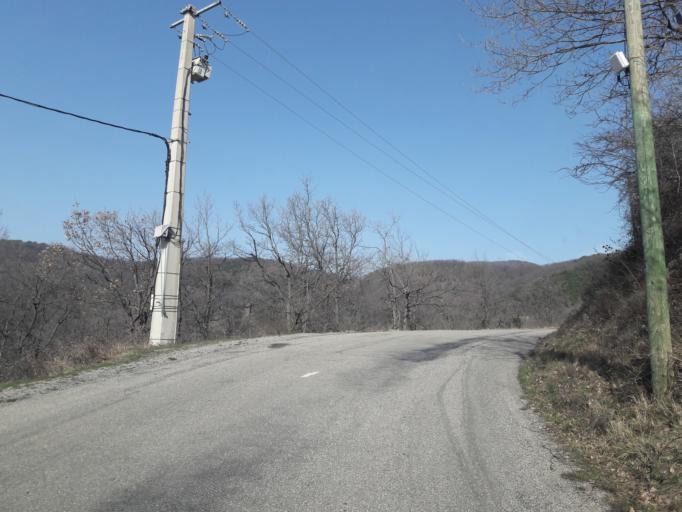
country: FR
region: Languedoc-Roussillon
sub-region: Departement du Gard
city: Sumene
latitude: 43.9984
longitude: 3.7693
